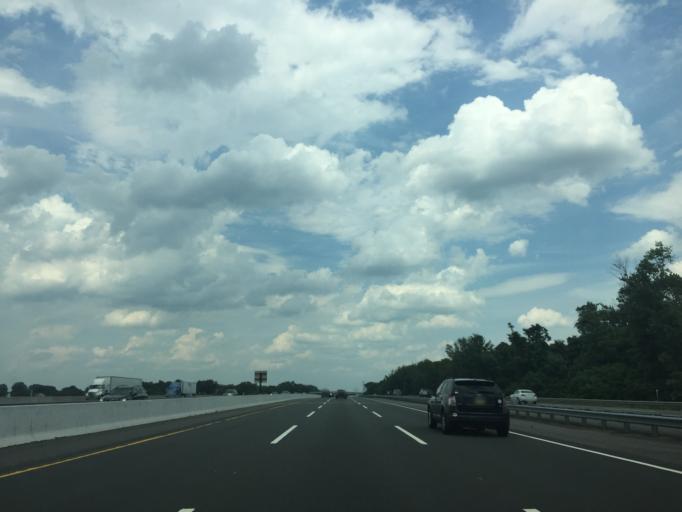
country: US
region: New Jersey
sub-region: Mercer County
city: Groveville
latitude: 40.1478
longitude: -74.6706
